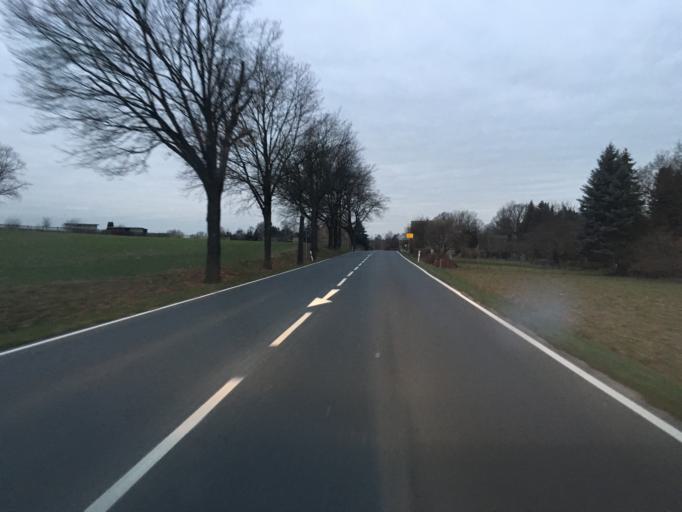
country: DE
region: Saxony
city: Dahlen
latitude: 51.3267
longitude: 13.0176
